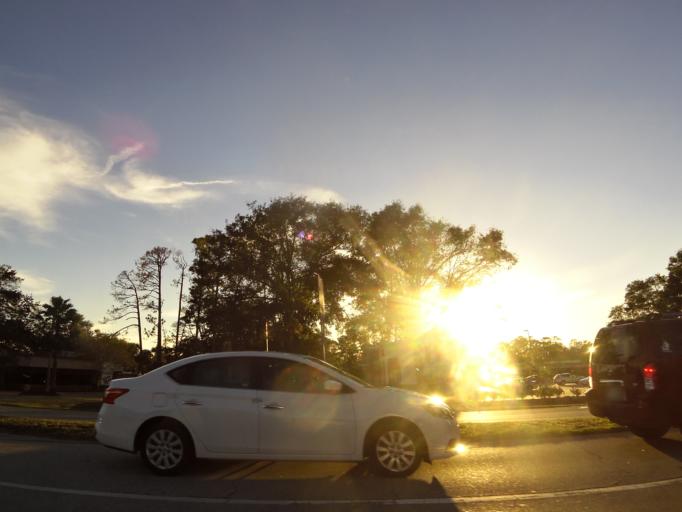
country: US
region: Florida
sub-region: Flagler County
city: Palm Coast
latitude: 29.5561
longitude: -81.2121
